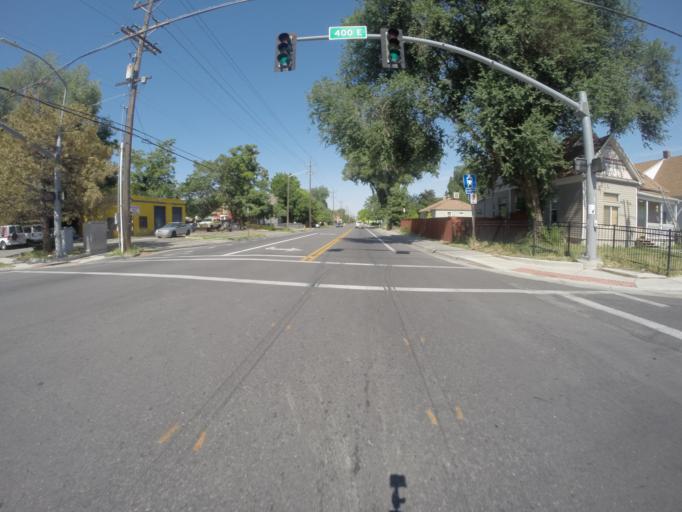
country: US
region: Utah
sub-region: Salt Lake County
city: Salt Lake City
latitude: 40.7417
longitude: -111.8796
